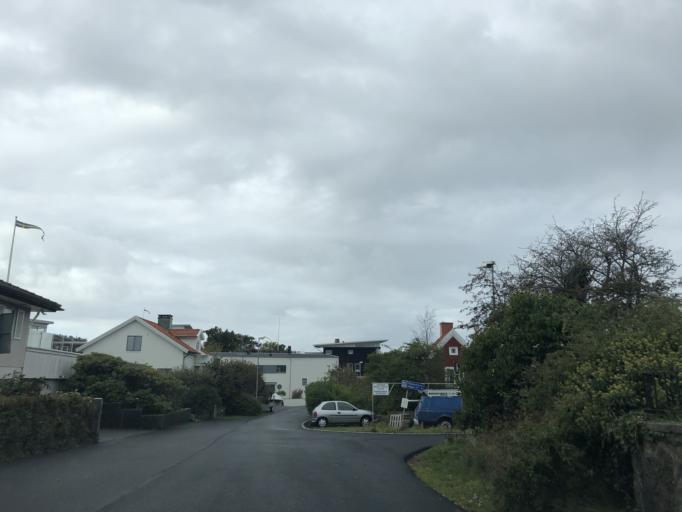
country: SE
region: Vaestra Goetaland
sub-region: Goteborg
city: Majorna
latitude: 57.6656
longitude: 11.8510
